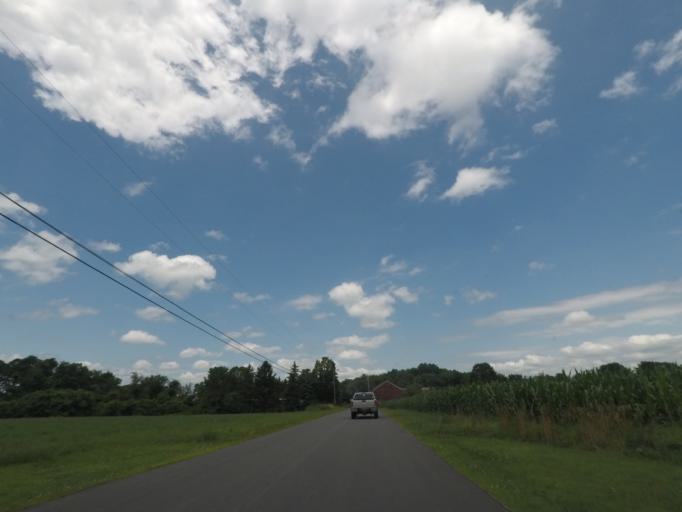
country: US
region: New York
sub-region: Rensselaer County
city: East Greenbush
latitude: 42.5343
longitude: -73.6901
